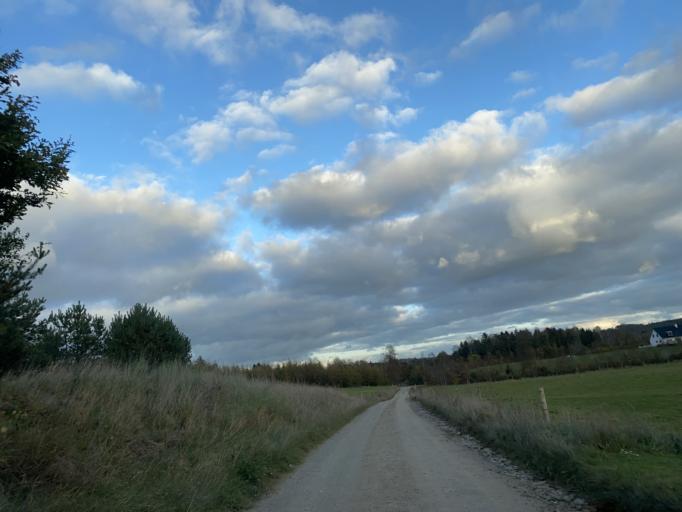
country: DK
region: Central Jutland
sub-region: Silkeborg Kommune
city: Svejbaek
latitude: 56.1786
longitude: 9.6160
